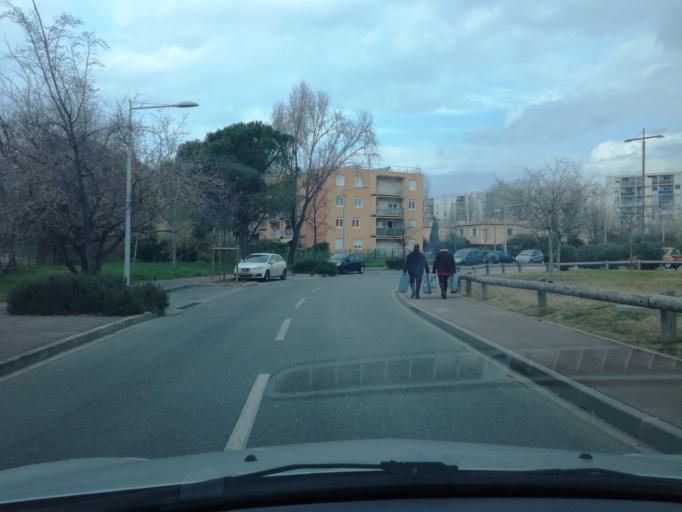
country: FR
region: Provence-Alpes-Cote d'Azur
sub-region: Departement des Alpes-Maritimes
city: Mandelieu-la-Napoule
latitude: 43.5545
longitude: 6.9635
